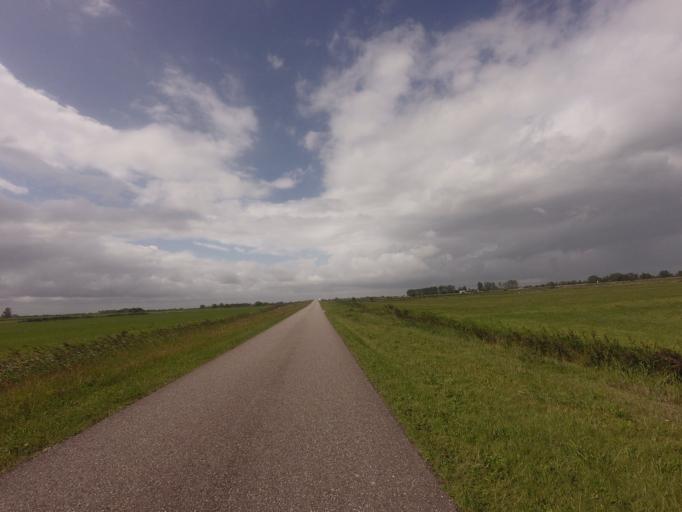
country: NL
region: Friesland
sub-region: Sudwest Fryslan
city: Oppenhuizen
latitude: 52.9784
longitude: 5.7373
